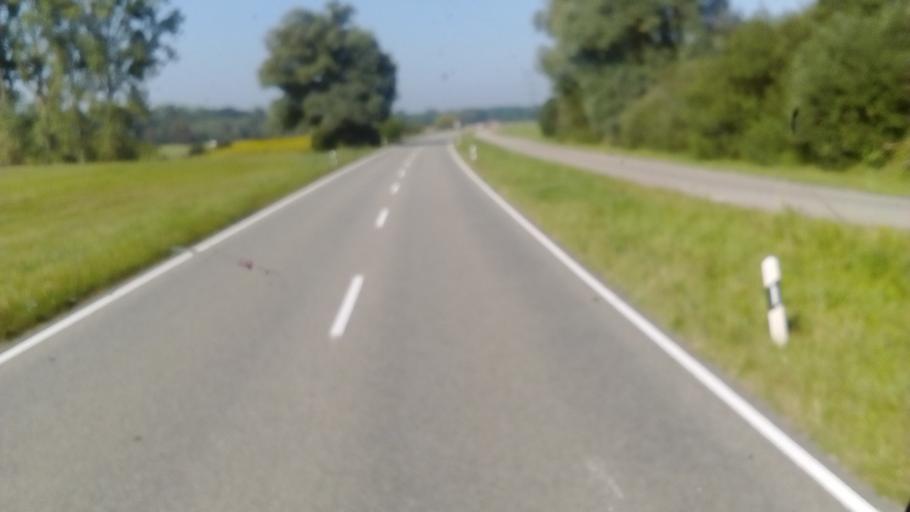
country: DE
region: Baden-Wuerttemberg
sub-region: Freiburg Region
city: Rheinau
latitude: 48.6514
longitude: 7.9727
